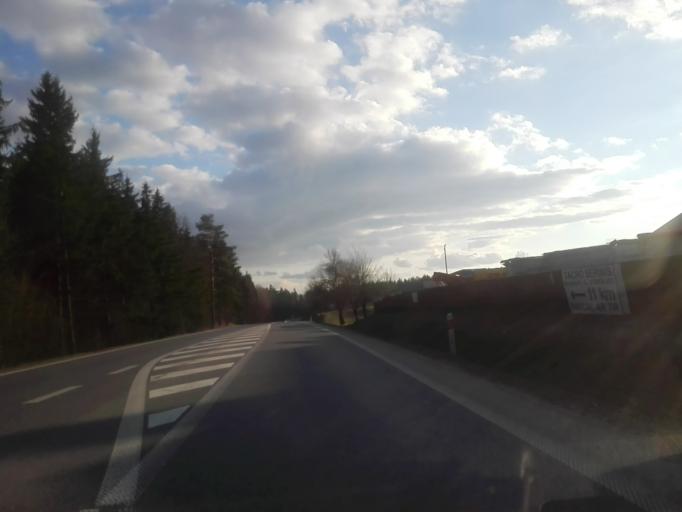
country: PL
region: Podlasie
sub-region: Suwalki
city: Suwalki
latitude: 54.1574
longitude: 22.9765
